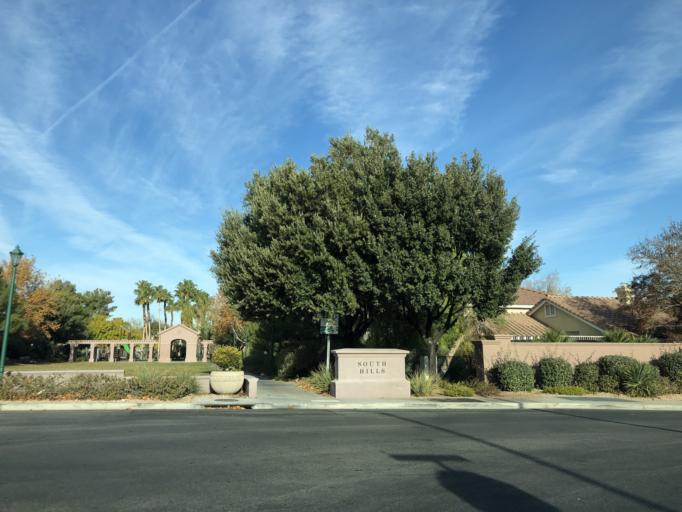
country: US
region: Nevada
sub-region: Clark County
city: Whitney
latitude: 36.0233
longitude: -115.0717
